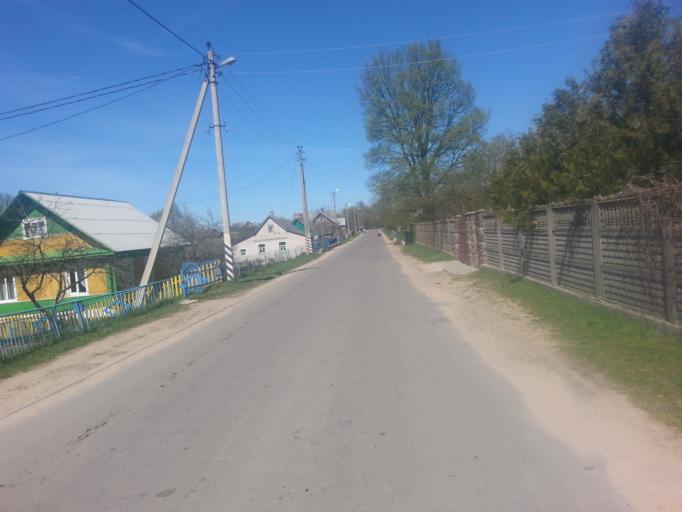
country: BY
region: Minsk
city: Narach
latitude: 54.9381
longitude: 26.6904
